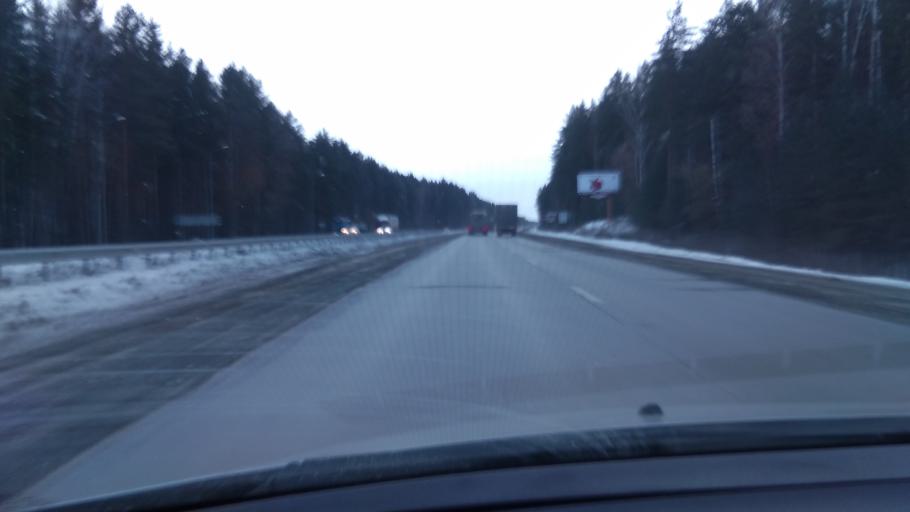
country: RU
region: Sverdlovsk
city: Sysert'
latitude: 56.5716
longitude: 60.8610
